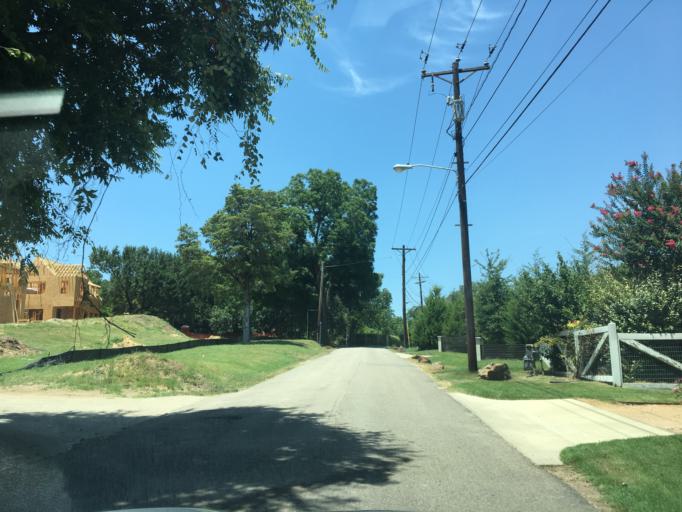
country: US
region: Texas
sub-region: Dallas County
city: Highland Park
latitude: 32.8385
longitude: -96.7322
